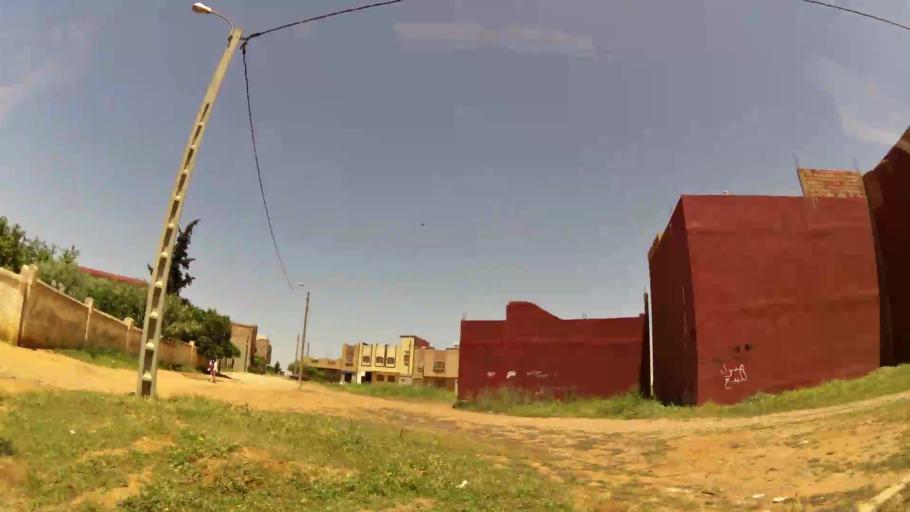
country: MA
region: Rabat-Sale-Zemmour-Zaer
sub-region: Khemisset
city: Khemisset
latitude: 33.8343
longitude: -6.0890
